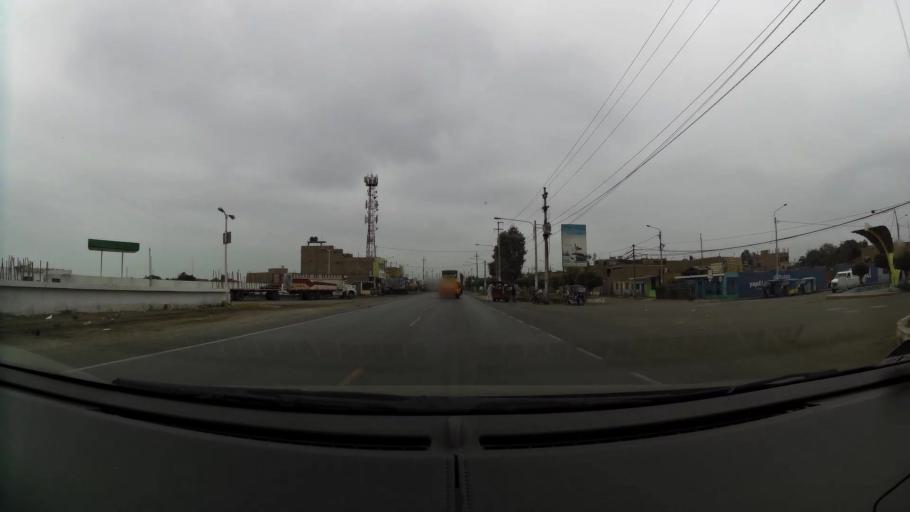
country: PE
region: Ancash
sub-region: Provincia de Santa
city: Santa
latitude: -8.9908
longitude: -78.6174
